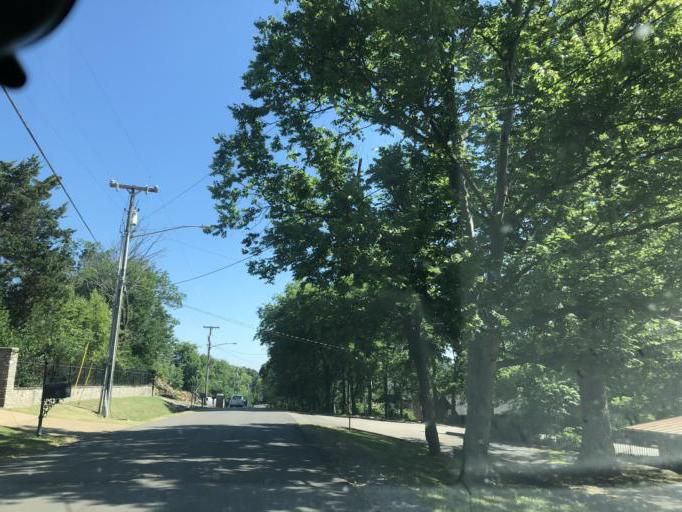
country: US
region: Tennessee
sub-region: Davidson County
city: Oak Hill
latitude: 36.1140
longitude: -86.8061
